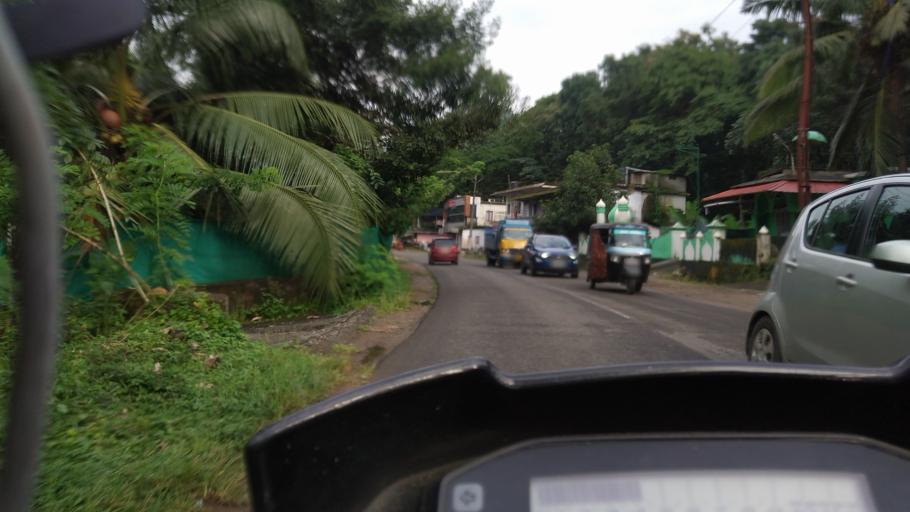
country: IN
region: Kerala
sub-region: Idukki
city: Kuttampuzha
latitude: 10.0513
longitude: 76.7440
